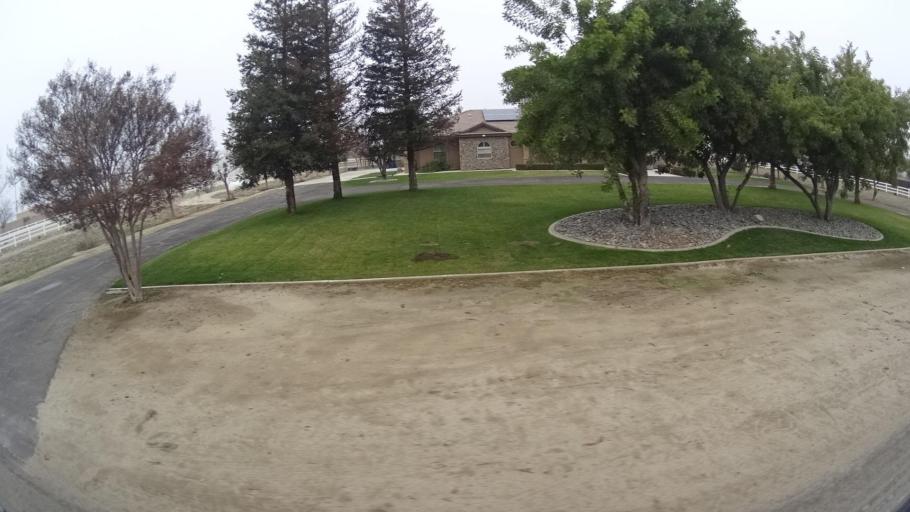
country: US
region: California
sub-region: Kern County
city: Greenfield
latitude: 35.2380
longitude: -119.0938
